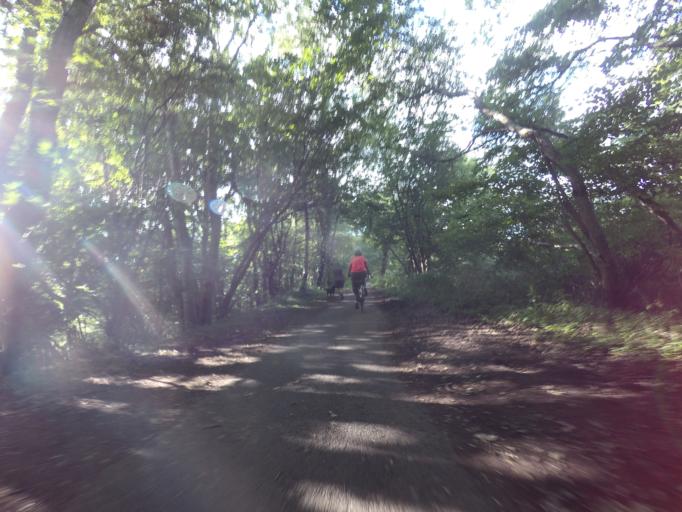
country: GB
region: England
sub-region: East Sussex
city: Horam
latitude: 50.9195
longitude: 0.2555
